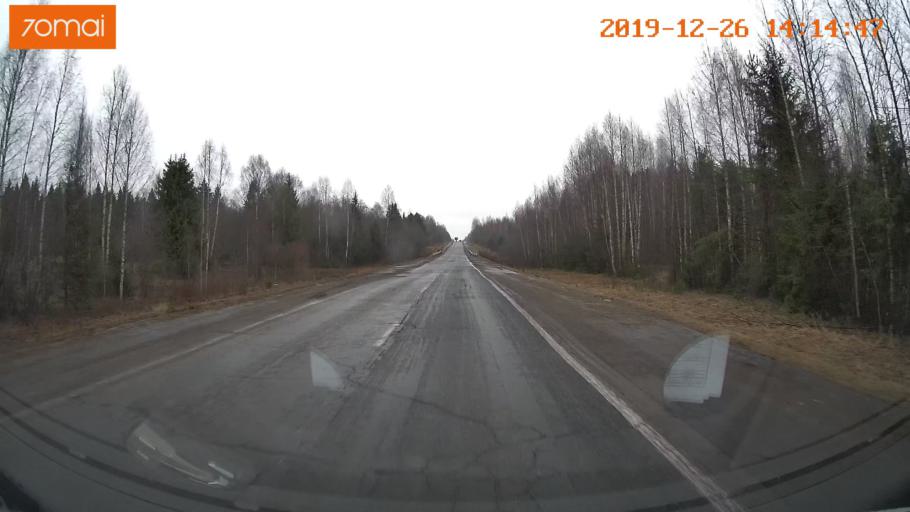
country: RU
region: Jaroslavl
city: Poshekhon'ye
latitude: 58.5146
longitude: 39.0339
